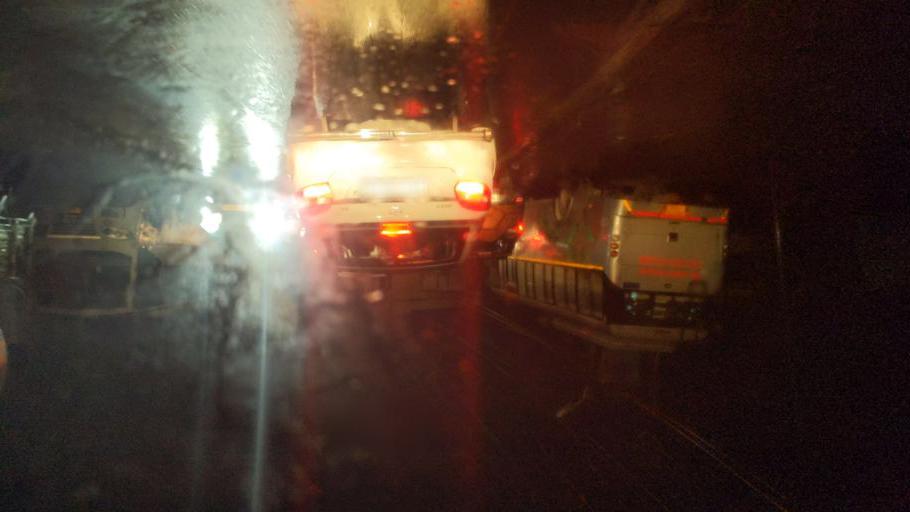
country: IN
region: Uttarakhand
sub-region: Naini Tal
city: Haldwani
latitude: 29.2727
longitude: 79.5449
